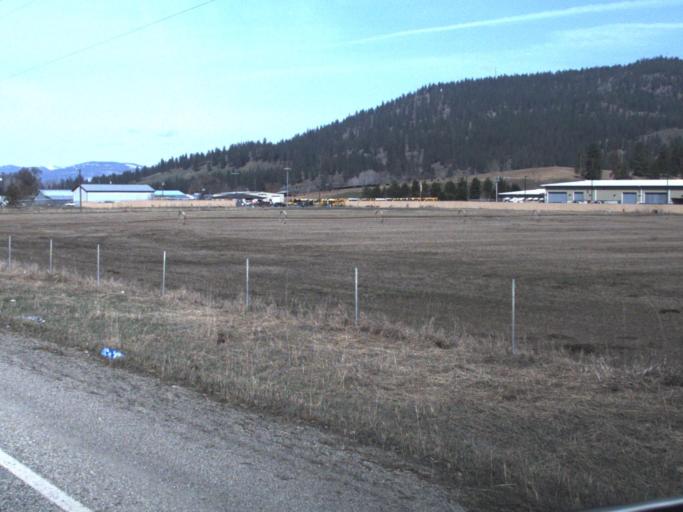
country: US
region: Washington
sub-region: Stevens County
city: Colville
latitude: 48.5474
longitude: -117.8711
